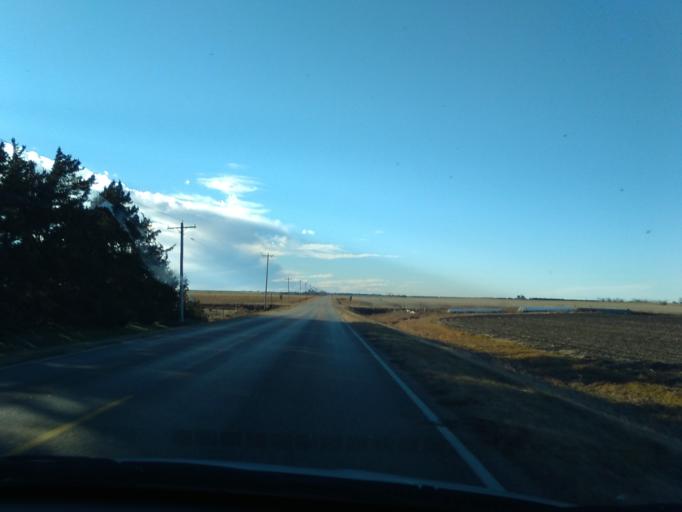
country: US
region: Nebraska
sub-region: Kearney County
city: Minden
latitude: 40.3651
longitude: -99.1018
